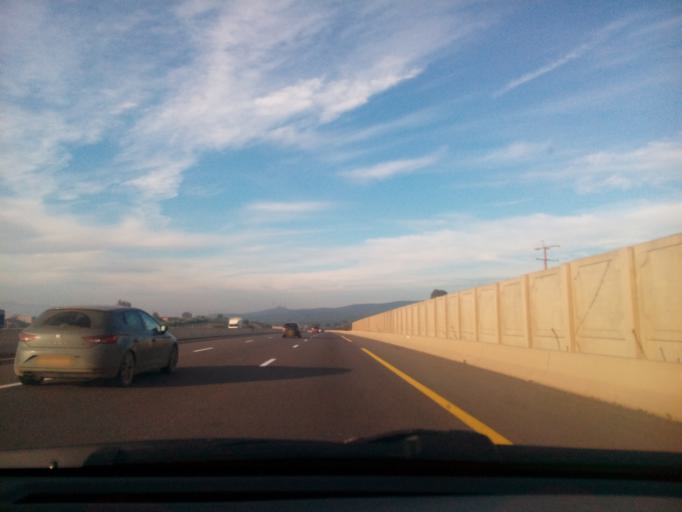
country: DZ
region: Relizane
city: Relizane
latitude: 35.7150
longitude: 0.2788
